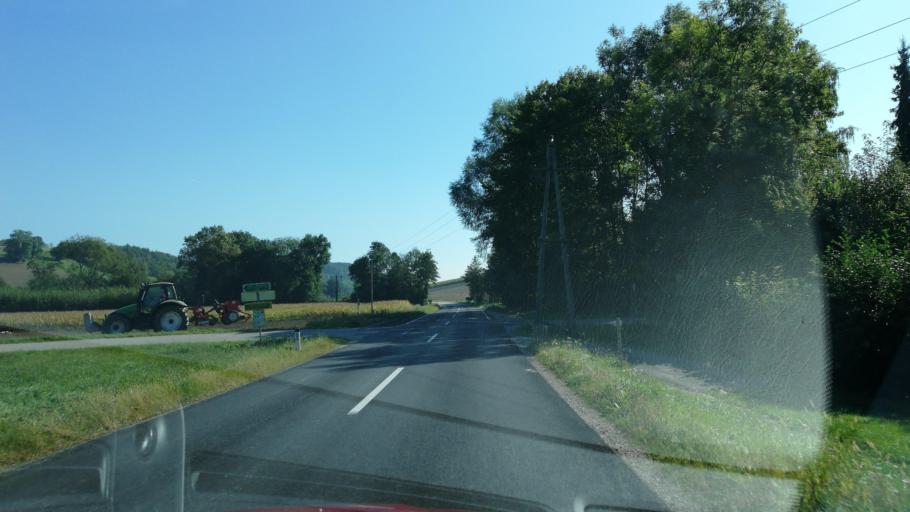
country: AT
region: Upper Austria
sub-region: Politischer Bezirk Grieskirchen
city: Grieskirchen
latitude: 48.2001
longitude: 13.8674
